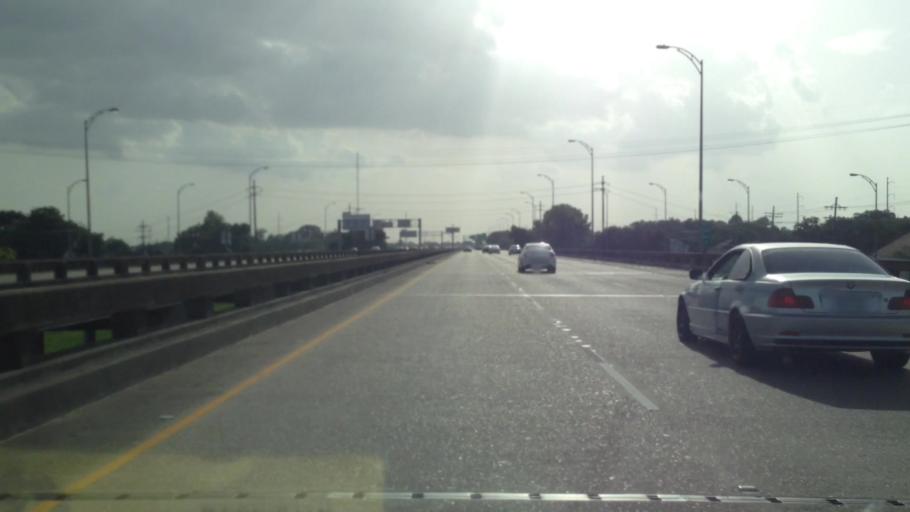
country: US
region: Louisiana
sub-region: Orleans Parish
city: New Orleans
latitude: 29.9914
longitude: -90.0589
